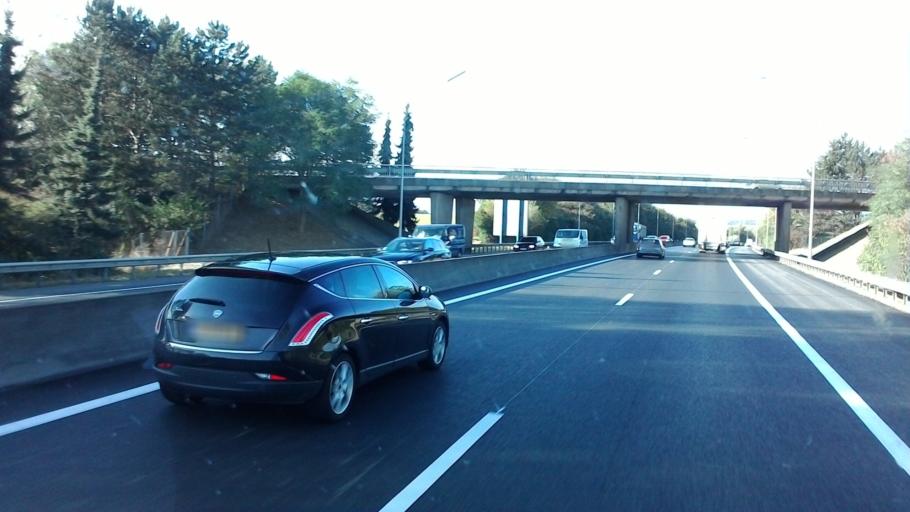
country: LU
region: Luxembourg
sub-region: Canton de Luxembourg
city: Strassen
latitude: 49.5945
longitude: 6.0809
